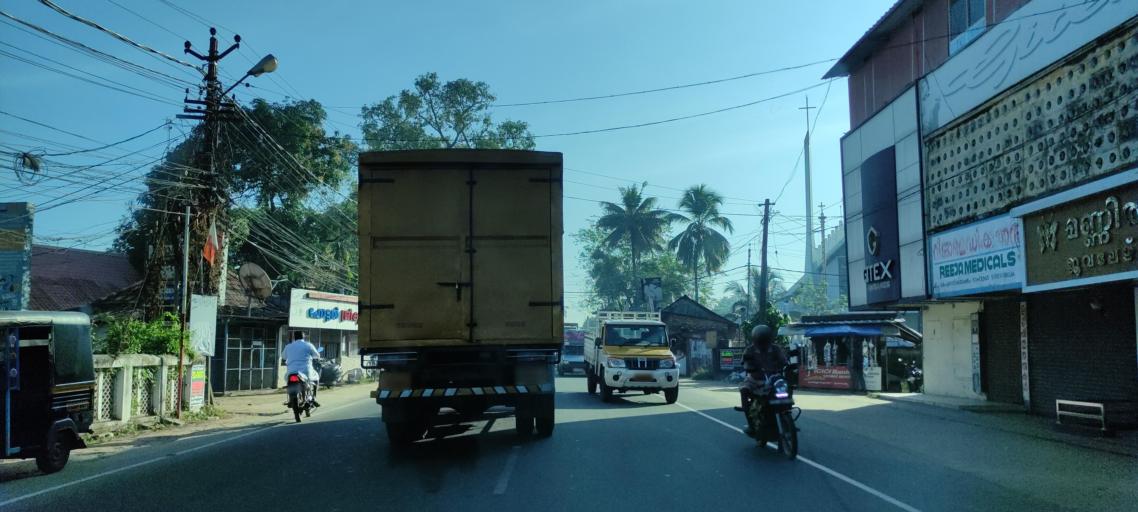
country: IN
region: Kerala
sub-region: Alappuzha
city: Kayankulam
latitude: 9.1749
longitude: 76.5020
